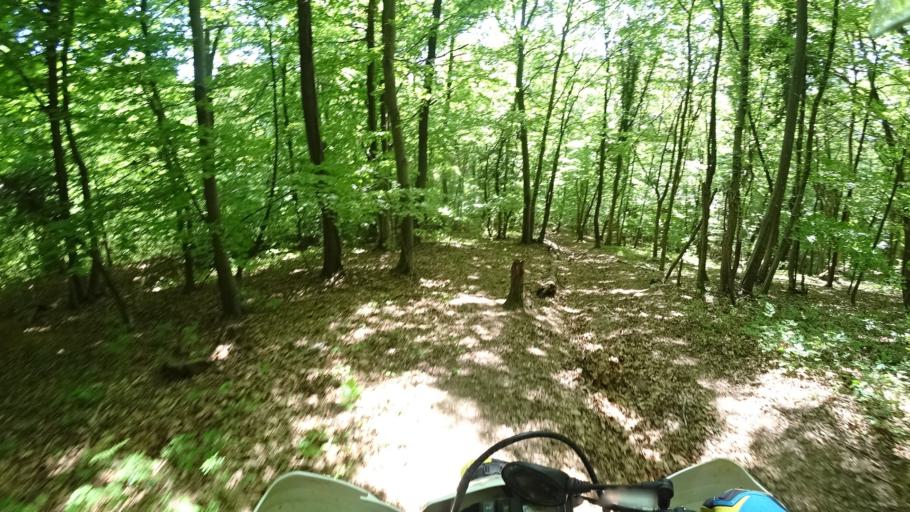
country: HR
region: Zagrebacka
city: Jablanovec
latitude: 45.8494
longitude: 15.8626
